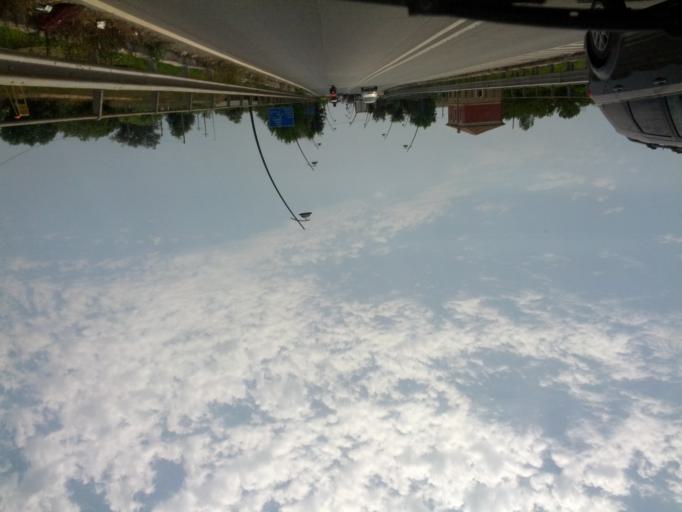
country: IT
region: Latium
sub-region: Provincia di Latina
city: Fondi
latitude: 41.3125
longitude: 13.4020
